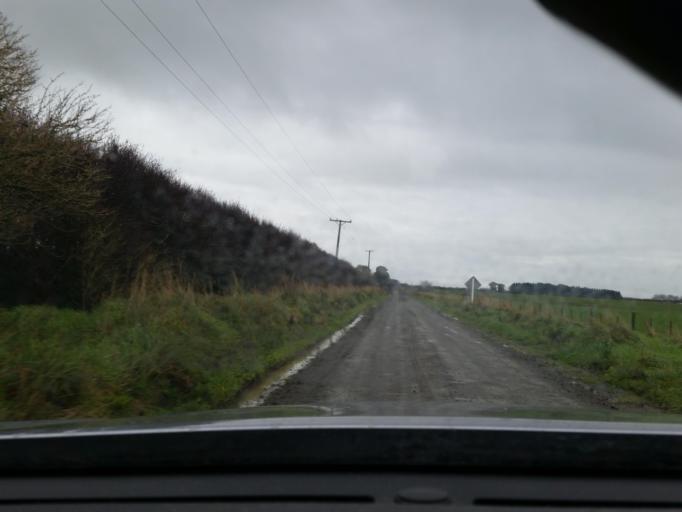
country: NZ
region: Southland
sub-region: Southland District
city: Riverton
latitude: -46.2412
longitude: 168.1211
